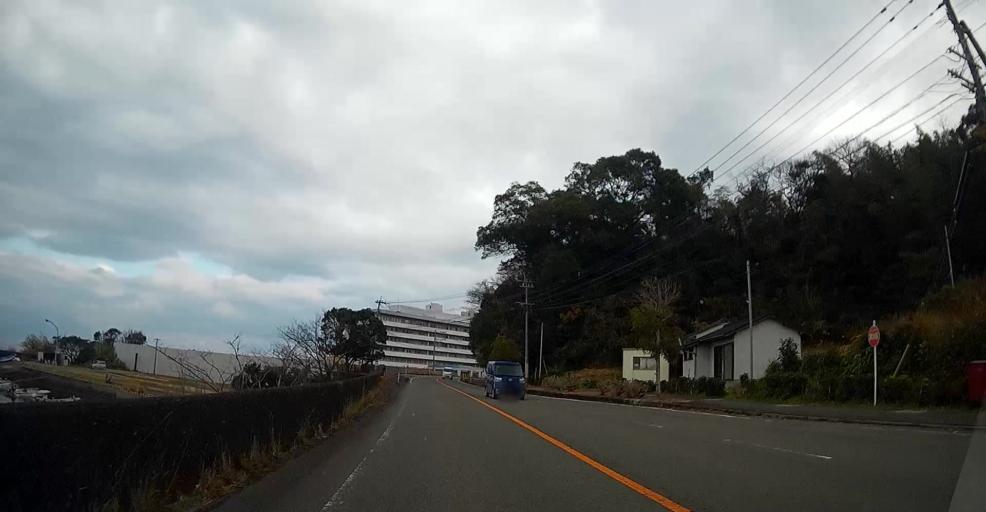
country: JP
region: Kumamoto
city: Hondo
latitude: 32.4813
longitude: 130.2729
